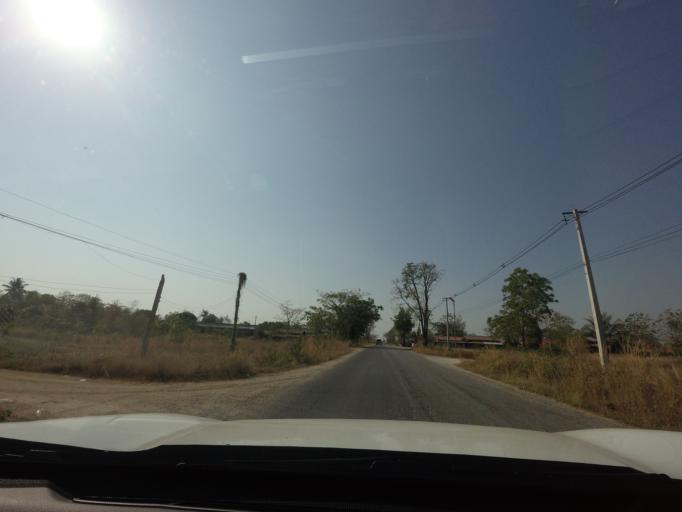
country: TH
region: Nakhon Ratchasima
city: Pak Chong
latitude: 14.6427
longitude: 101.4900
